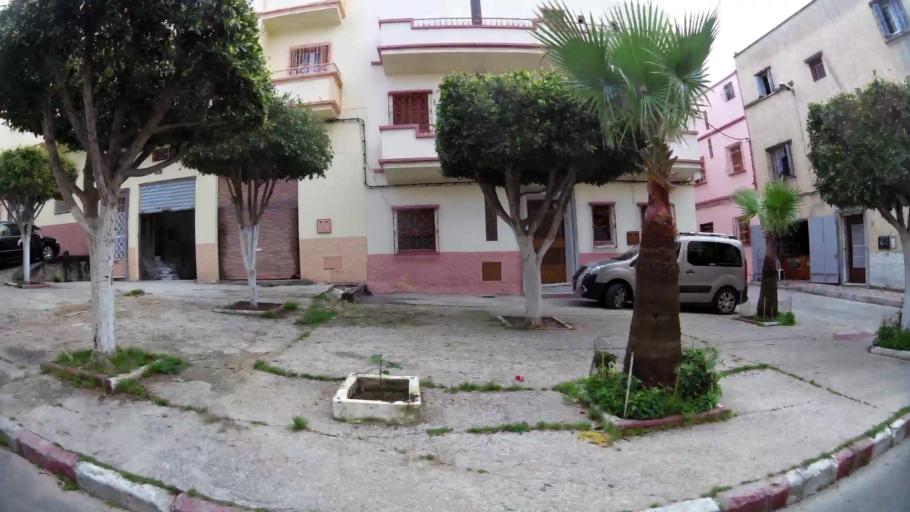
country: MA
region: Tanger-Tetouan
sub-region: Tanger-Assilah
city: Tangier
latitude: 35.7721
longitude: -5.8227
